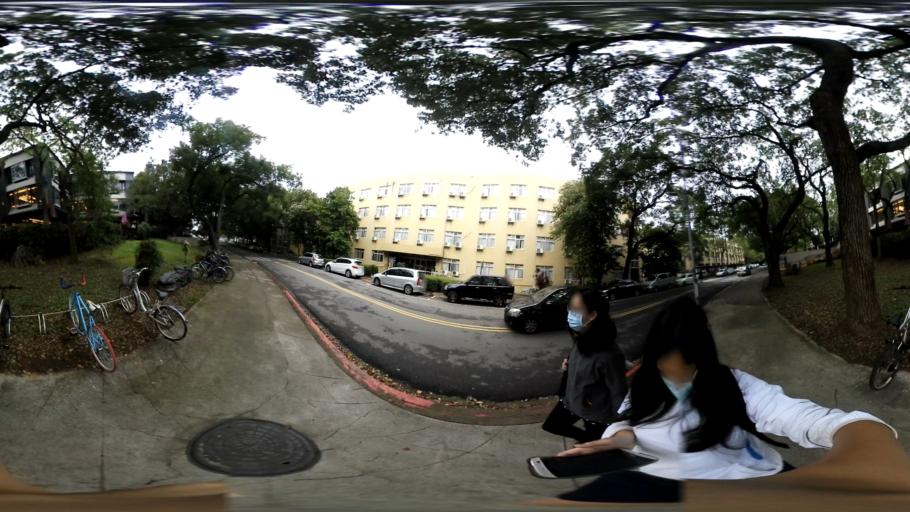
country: TW
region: Taiwan
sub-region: Hsinchu
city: Hsinchu
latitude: 24.7896
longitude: 120.9975
